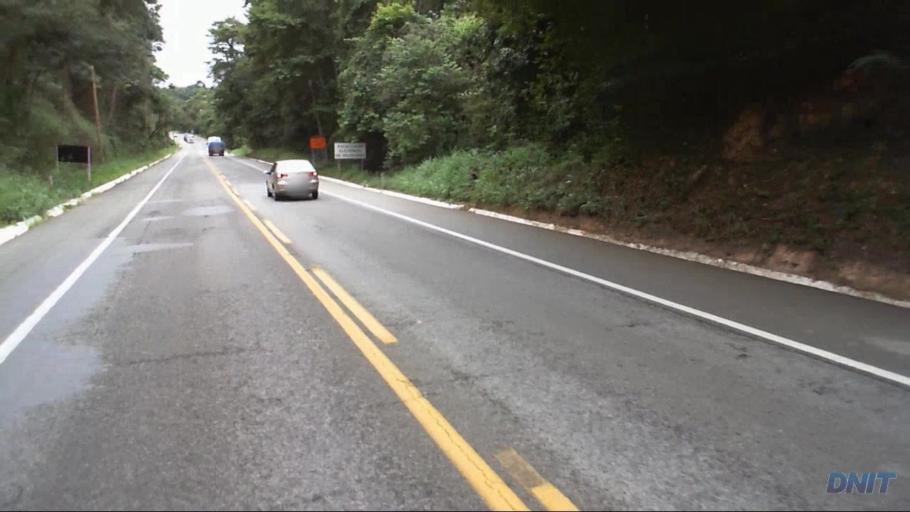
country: BR
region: Minas Gerais
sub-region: Barao De Cocais
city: Barao de Cocais
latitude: -19.8028
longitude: -43.4100
